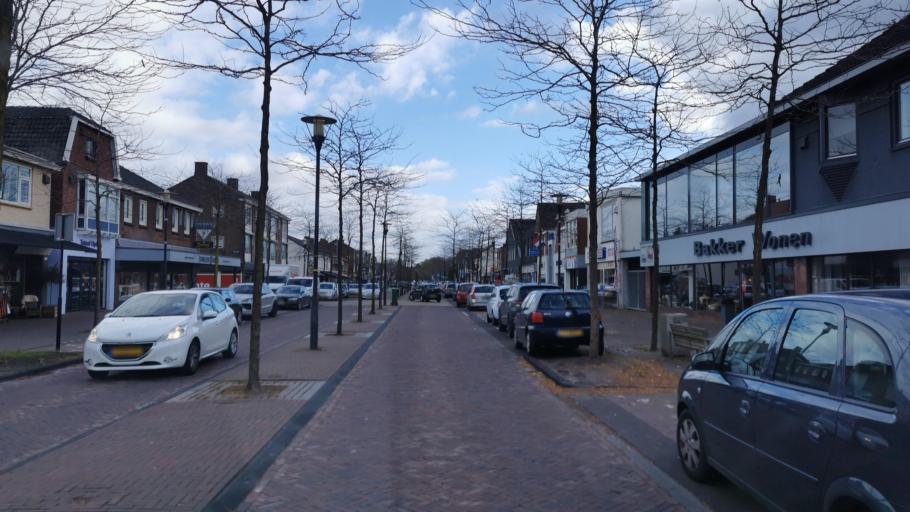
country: DE
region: North Rhine-Westphalia
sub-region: Regierungsbezirk Munster
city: Gronau
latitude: 52.2156
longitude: 6.9686
